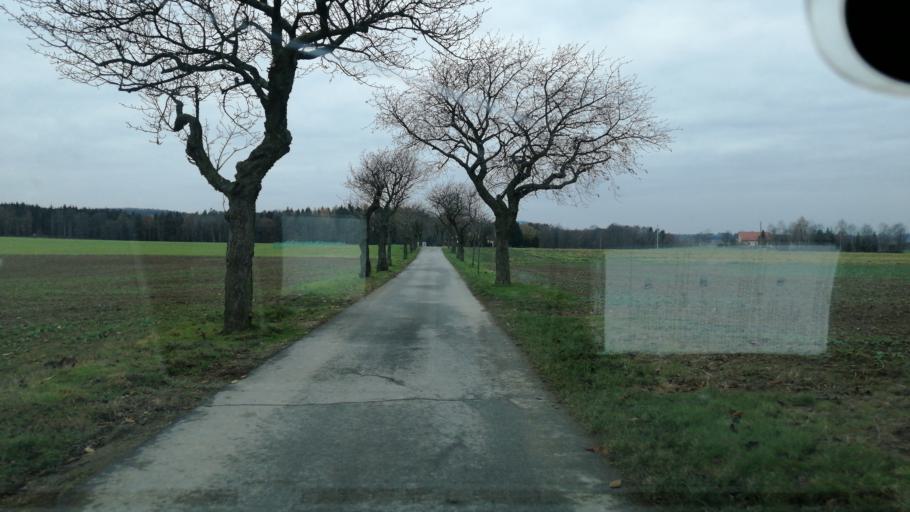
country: DE
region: Saxony
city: Bernstadt
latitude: 51.0535
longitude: 14.7919
